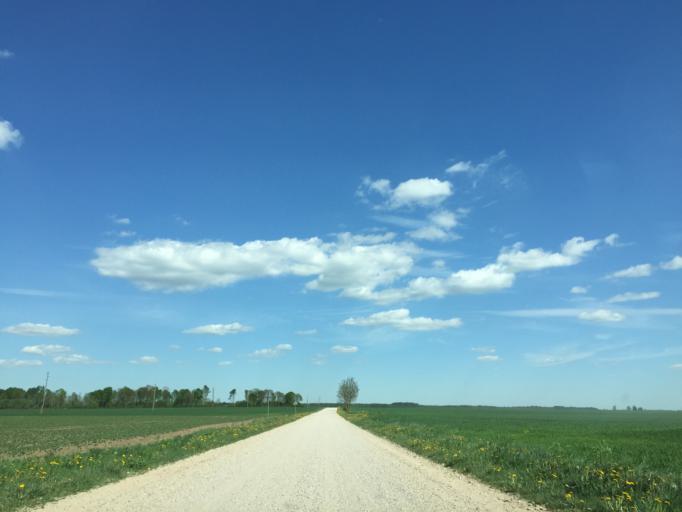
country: LV
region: Rundales
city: Pilsrundale
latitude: 56.3533
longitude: 23.9648
